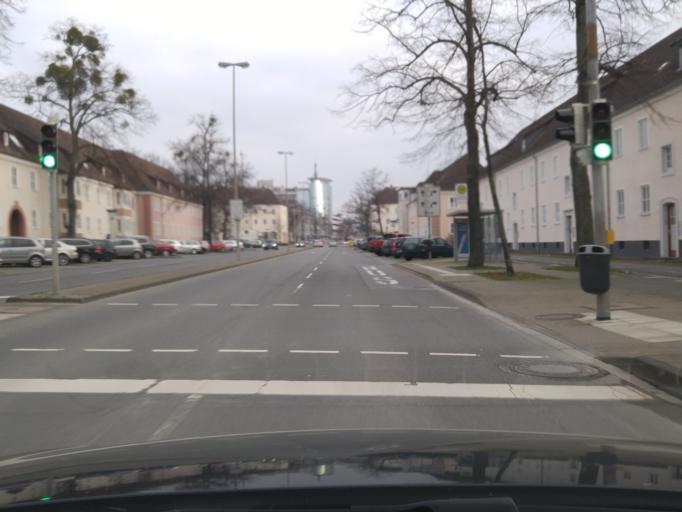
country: DE
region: Lower Saxony
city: Wolfsburg
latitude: 52.4226
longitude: 10.7808
